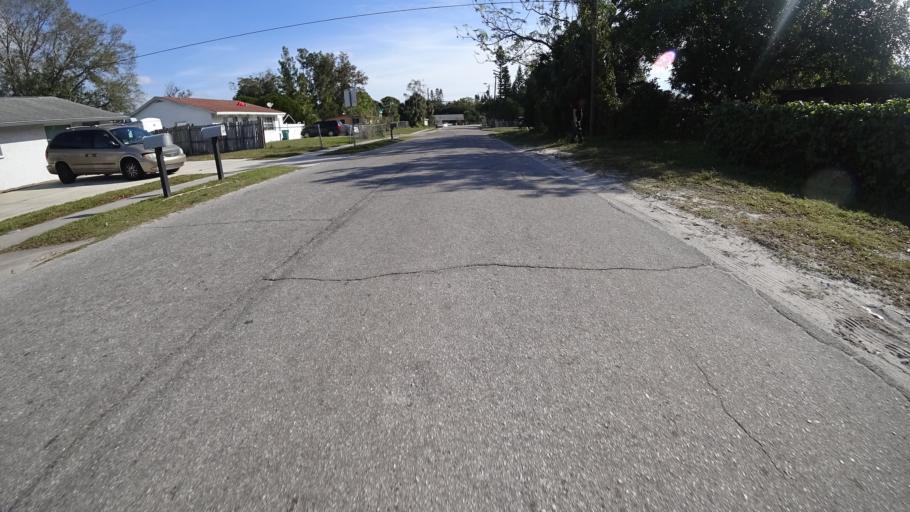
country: US
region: Florida
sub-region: Manatee County
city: Whitfield
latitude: 27.4349
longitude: -82.5642
